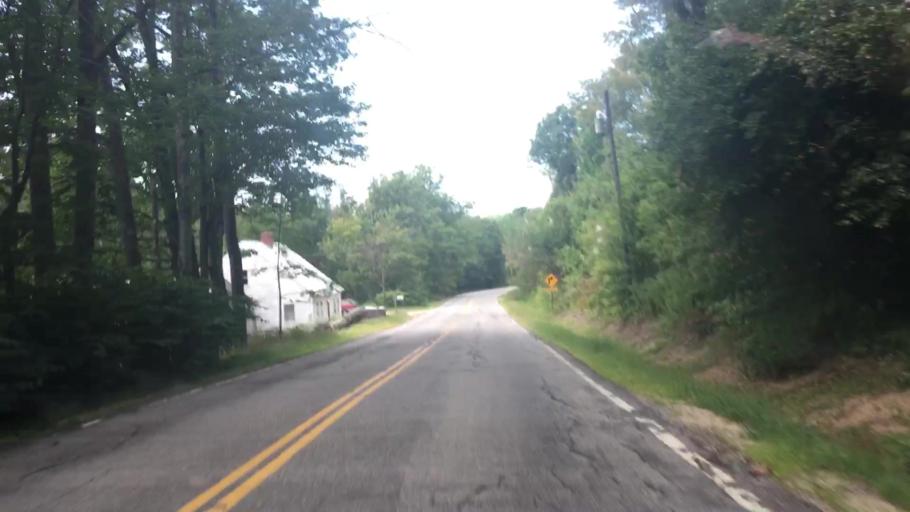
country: US
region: Maine
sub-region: Oxford County
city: Oxford
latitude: 44.0755
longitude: -70.5480
